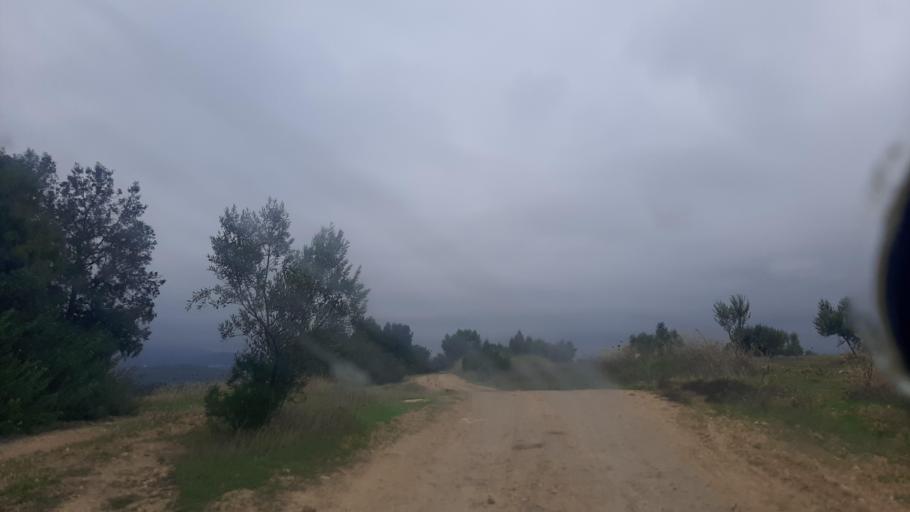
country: TN
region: Tunis
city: La Sebala du Mornag
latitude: 36.5746
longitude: 10.2929
